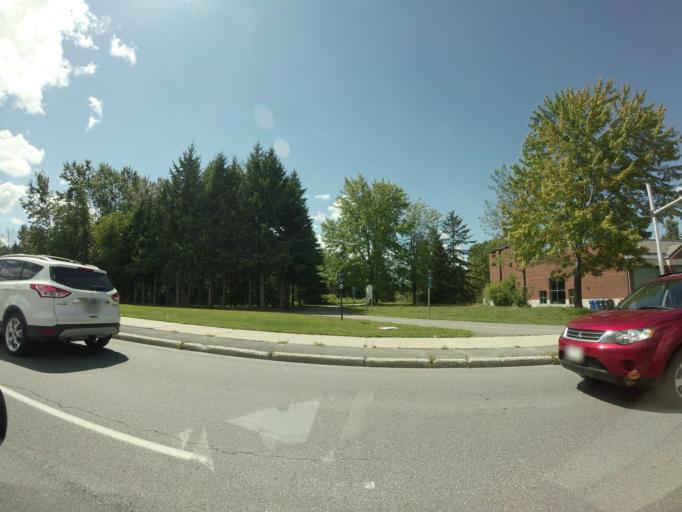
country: CA
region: Ontario
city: Bells Corners
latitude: 45.3527
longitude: -75.7638
